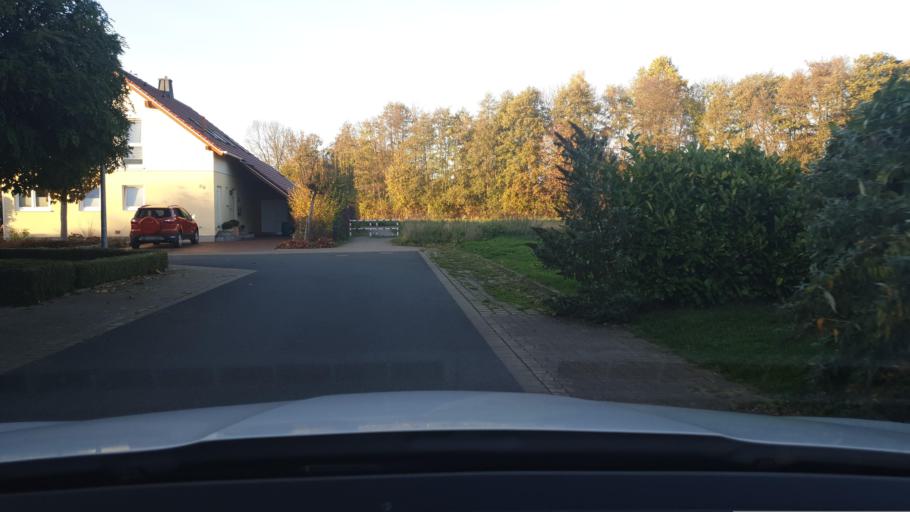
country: DE
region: North Rhine-Westphalia
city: Bad Oeynhausen
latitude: 52.2129
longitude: 8.7845
